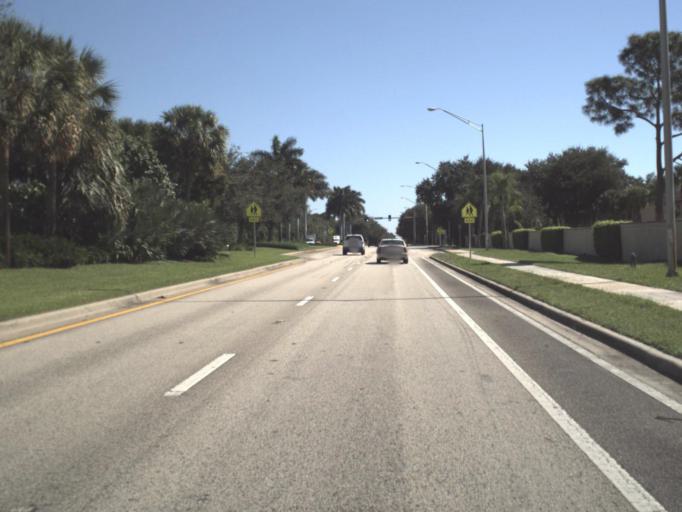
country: US
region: Florida
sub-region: Collier County
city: Naples
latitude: 26.1385
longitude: -81.7596
